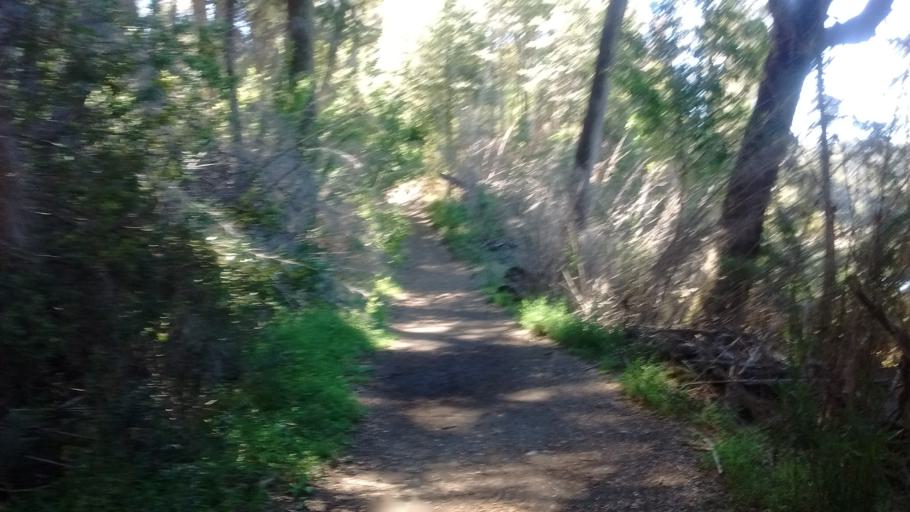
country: AR
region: Rio Negro
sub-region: Departamento de Bariloche
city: San Carlos de Bariloche
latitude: -41.0544
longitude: -71.5586
